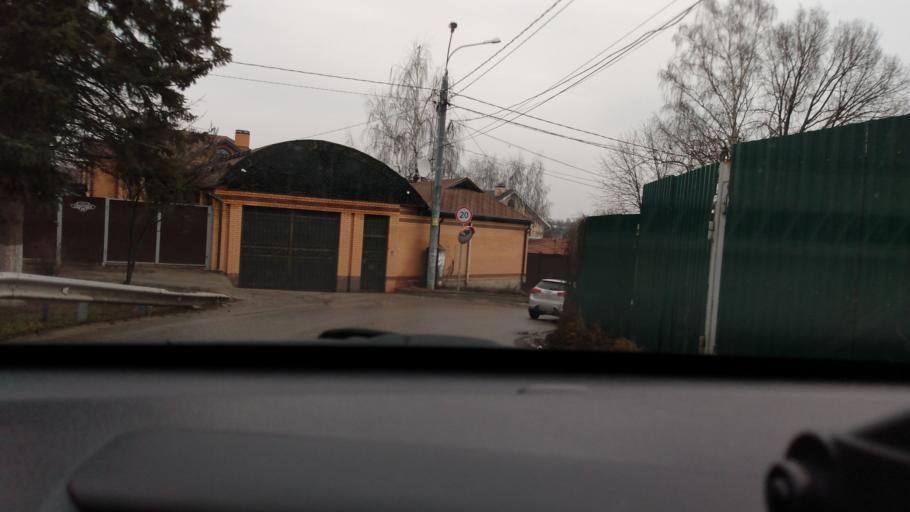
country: RU
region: Moscow
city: Zagor'ye
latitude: 55.5510
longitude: 37.6588
